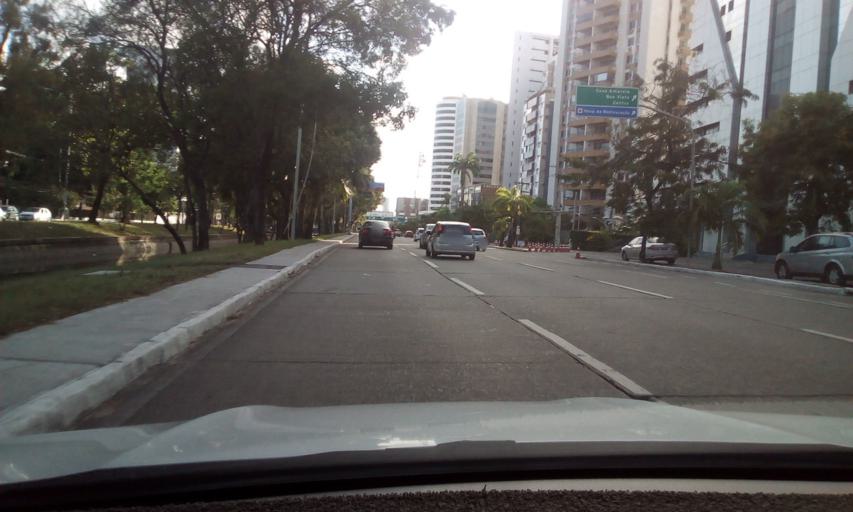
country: BR
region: Pernambuco
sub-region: Recife
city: Recife
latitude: -8.0465
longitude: -34.8914
